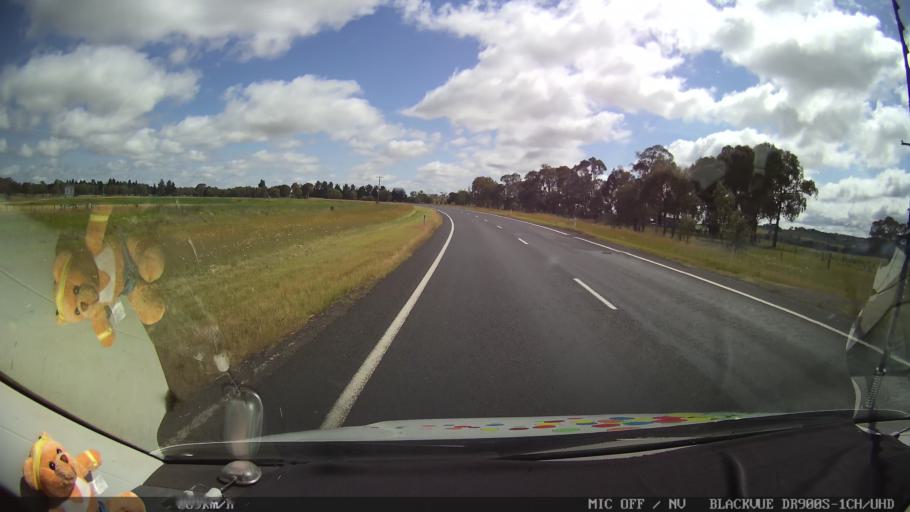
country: AU
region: New South Wales
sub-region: Glen Innes Severn
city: Glen Innes
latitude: -29.9120
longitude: 151.7308
